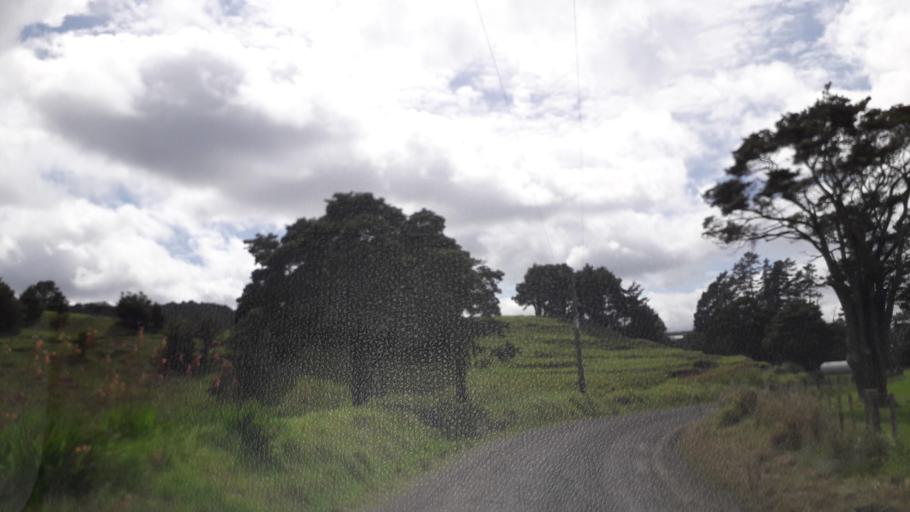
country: NZ
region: Northland
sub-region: Far North District
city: Ahipara
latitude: -35.2408
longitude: 173.2565
